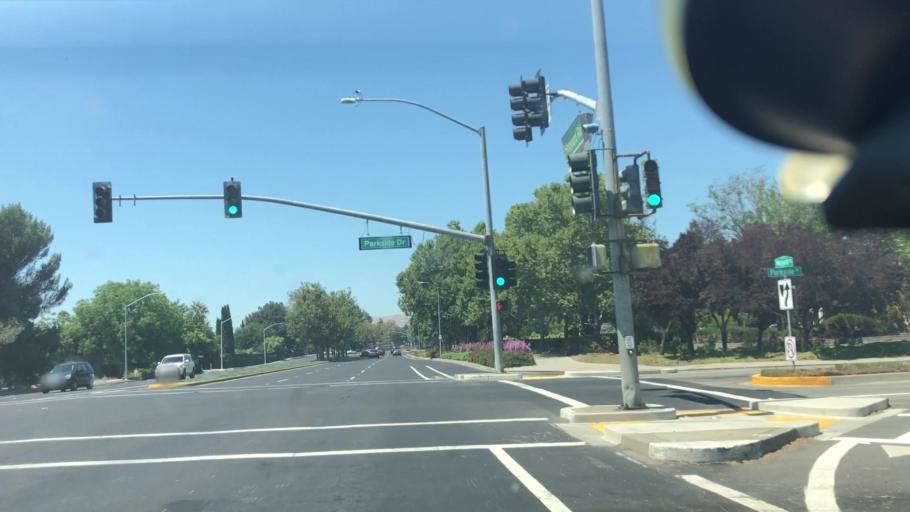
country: US
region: California
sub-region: Alameda County
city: Pleasanton
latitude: 37.6778
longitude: -121.8998
